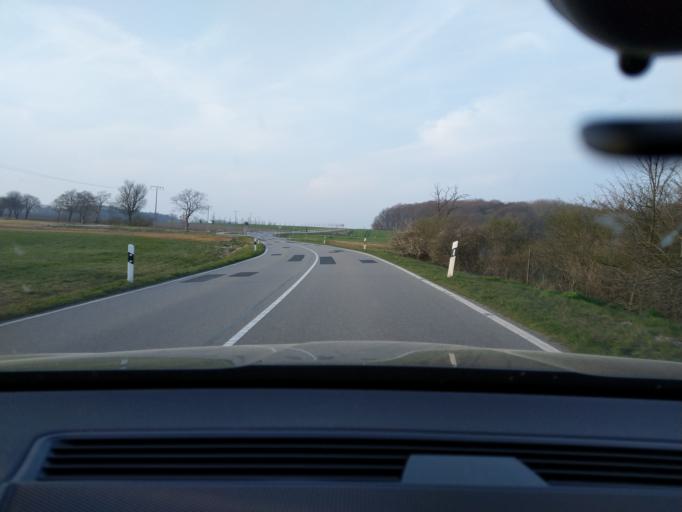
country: DE
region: Mecklenburg-Vorpommern
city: Kramerhof
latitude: 54.3362
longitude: 13.0303
